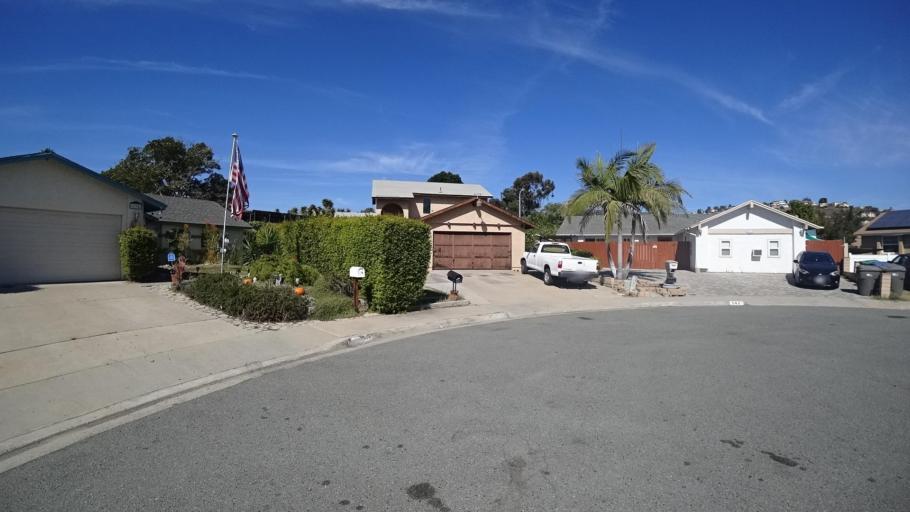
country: US
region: California
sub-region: San Diego County
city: La Presa
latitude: 32.7074
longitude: -116.9888
